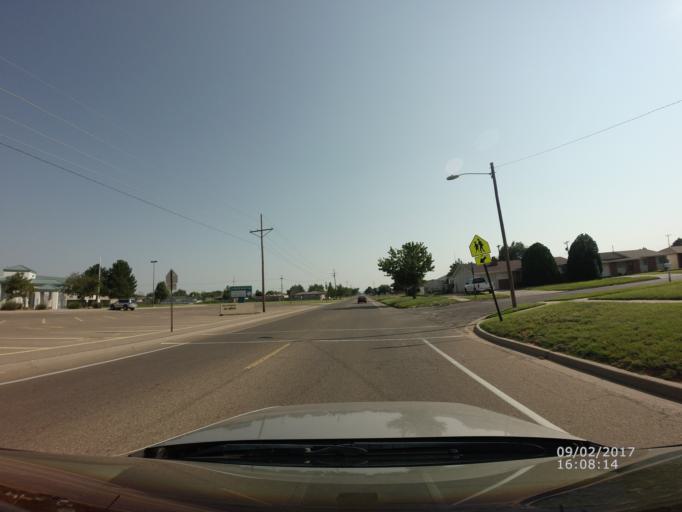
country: US
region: New Mexico
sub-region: Curry County
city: Clovis
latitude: 34.4314
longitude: -103.2141
